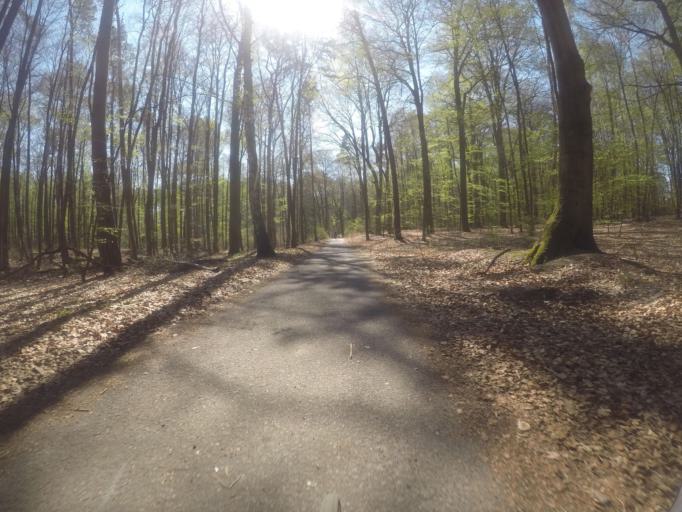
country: DE
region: Brandenburg
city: Wandlitz
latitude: 52.7499
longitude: 13.4940
